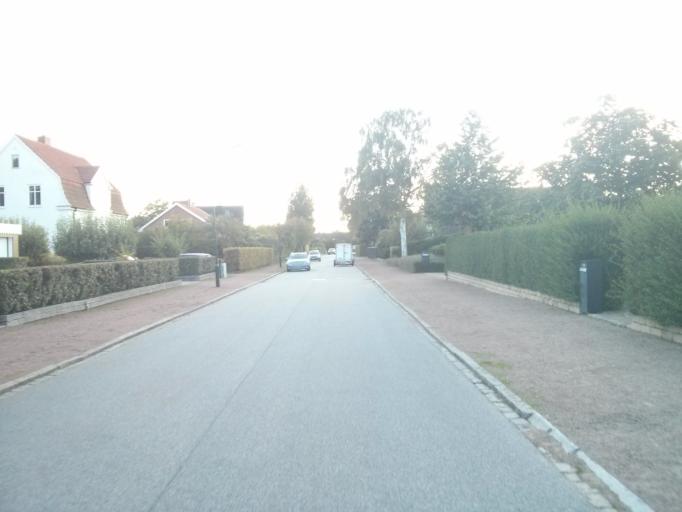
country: SE
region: Skane
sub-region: Malmo
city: Malmoe
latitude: 55.5851
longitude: 12.9674
